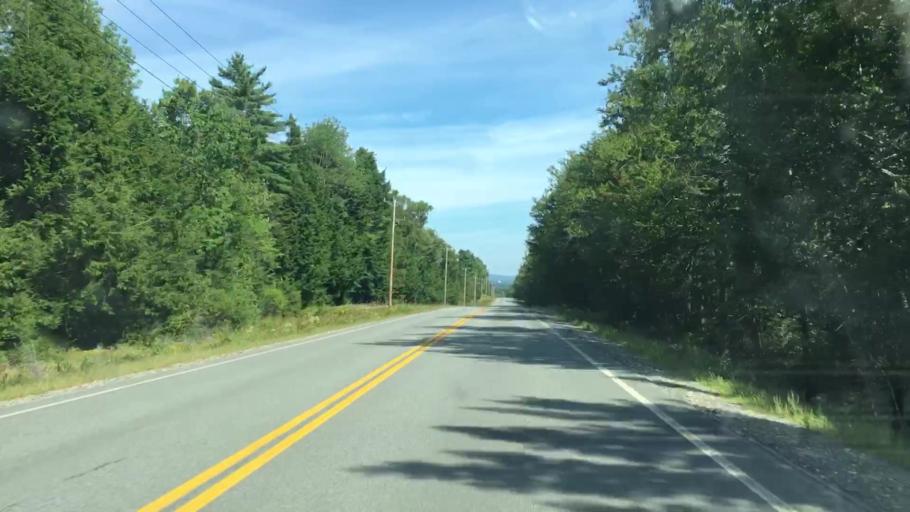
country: US
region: Maine
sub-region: Penobscot County
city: Howland
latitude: 45.2324
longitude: -68.7591
